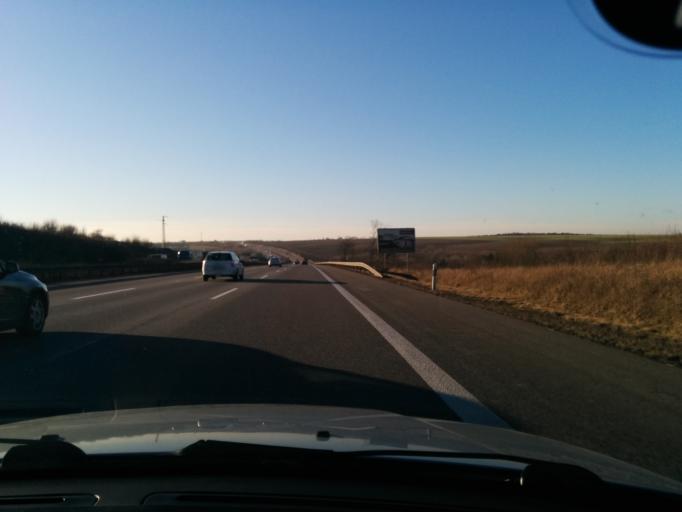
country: DE
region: Thuringia
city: Vollersroda
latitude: 50.9403
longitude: 11.3352
